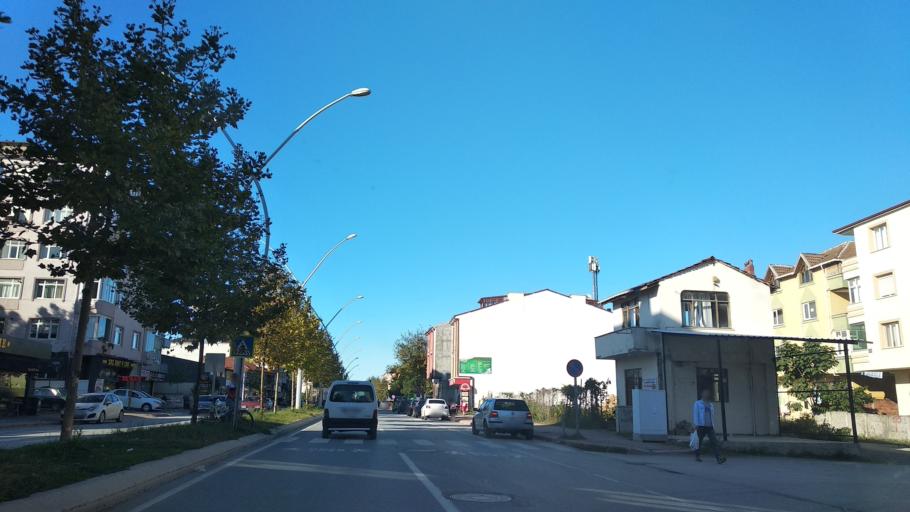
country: TR
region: Sakarya
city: Karasu
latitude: 41.1027
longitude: 30.6926
